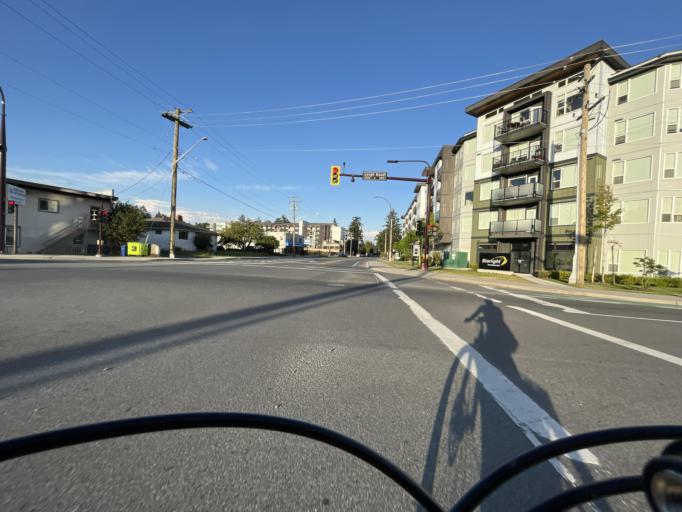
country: CA
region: British Columbia
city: Langford
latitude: 48.4496
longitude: -123.5183
